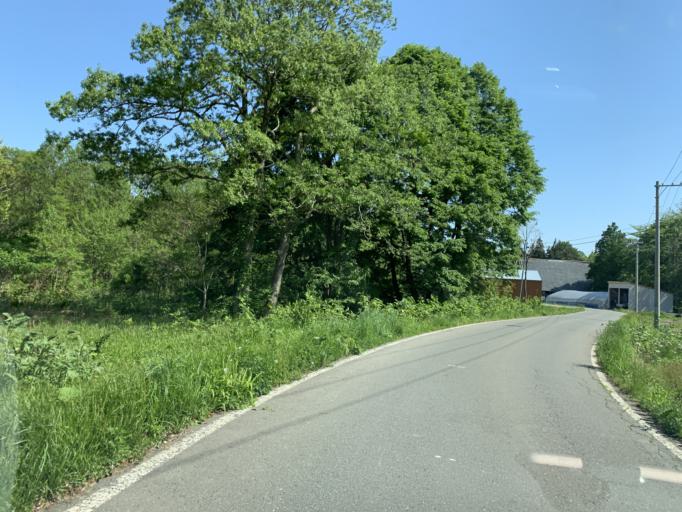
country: JP
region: Iwate
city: Shizukuishi
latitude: 39.5595
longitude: 140.8413
